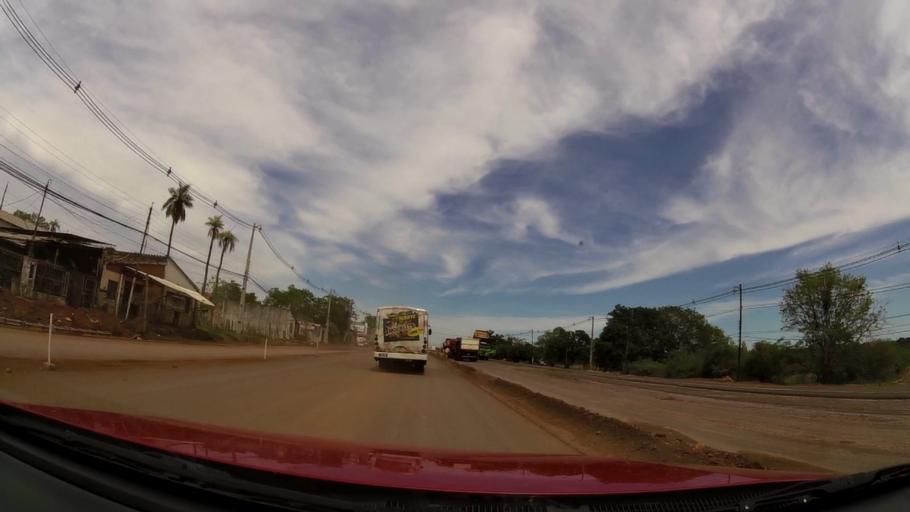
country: PY
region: Central
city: Limpio
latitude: -25.1936
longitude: -57.5079
